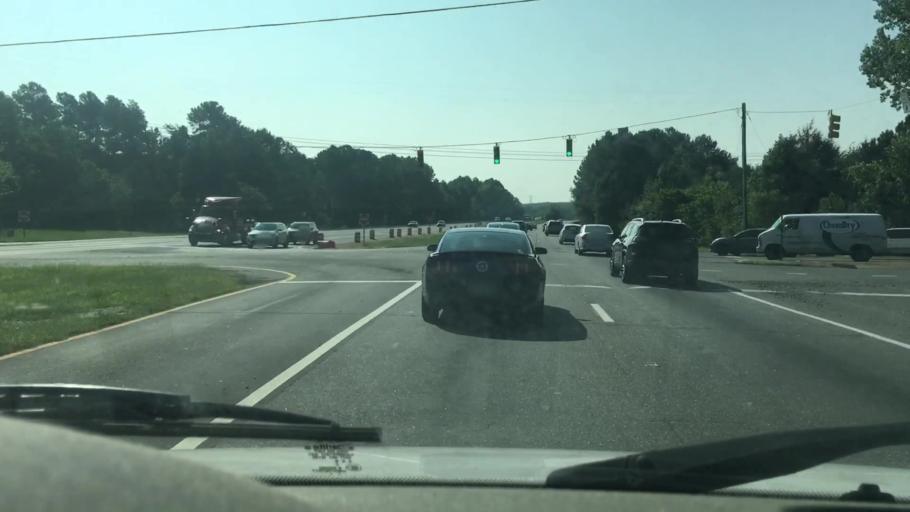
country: US
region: North Carolina
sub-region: Gaston County
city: Mount Holly
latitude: 35.3546
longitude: -80.9776
